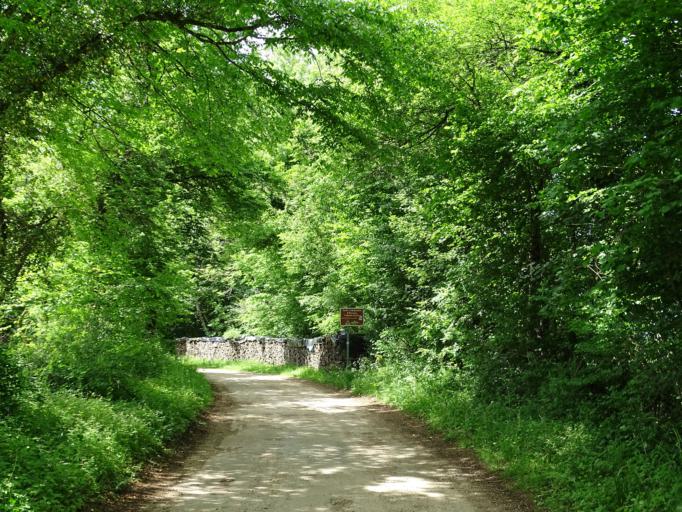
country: FR
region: Franche-Comte
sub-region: Departement du Doubs
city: Levier
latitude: 47.0096
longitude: 6.0156
